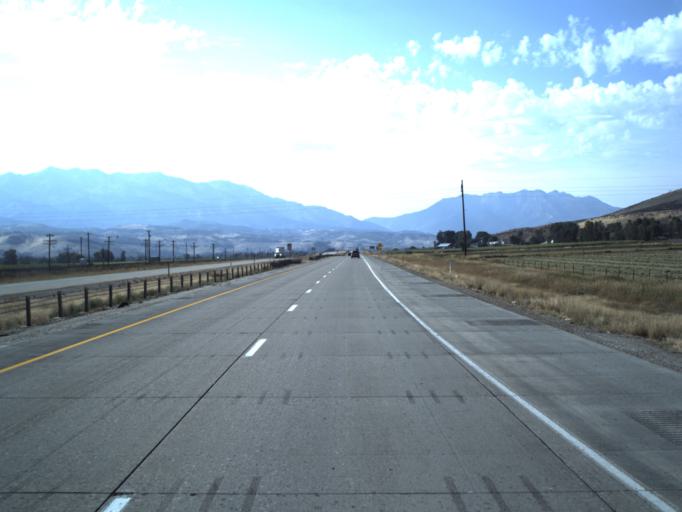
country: US
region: Utah
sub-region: Morgan County
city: Morgan
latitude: 41.0504
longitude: -111.6825
